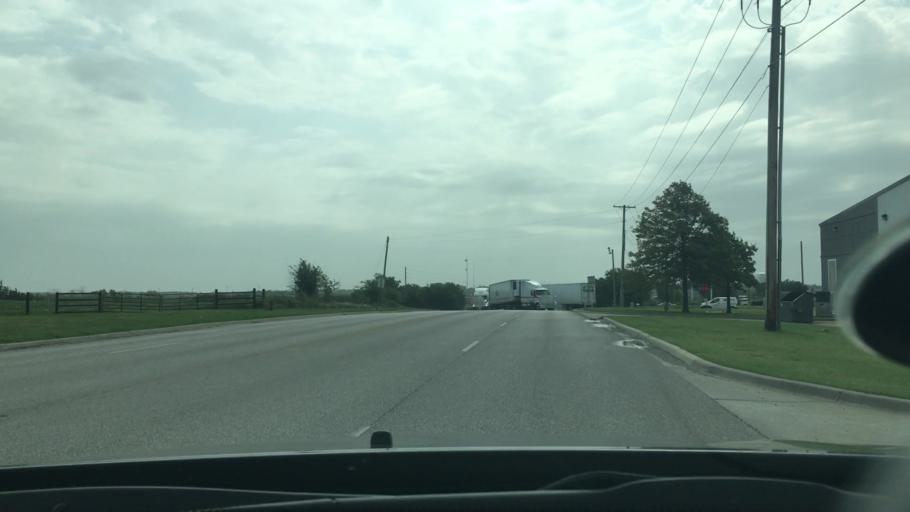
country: US
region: Oklahoma
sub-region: Carter County
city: Ardmore
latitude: 34.2019
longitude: -97.1697
